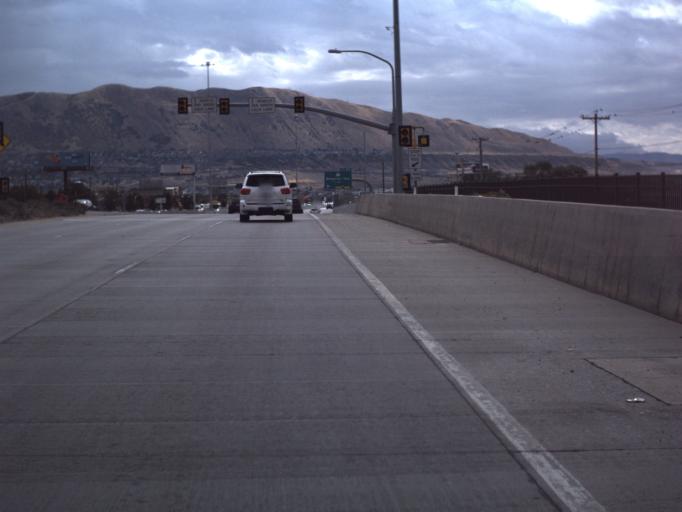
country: US
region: Utah
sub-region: Salt Lake County
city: Draper
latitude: 40.5249
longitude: -111.8917
